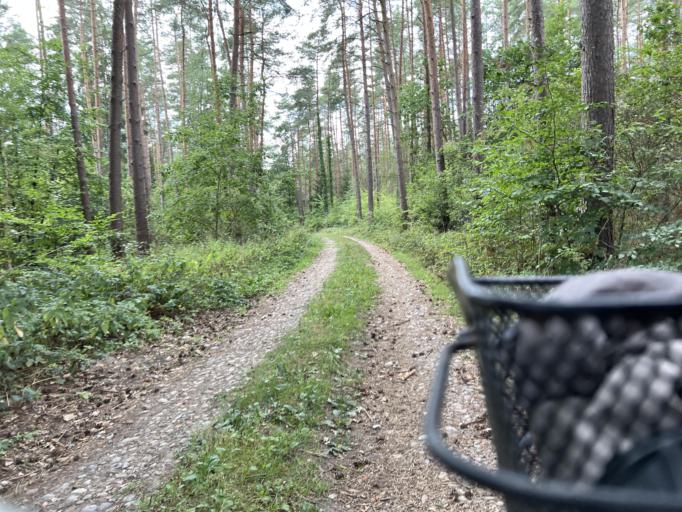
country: DE
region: Lower Saxony
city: Tosterglope
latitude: 53.2043
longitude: 10.8498
